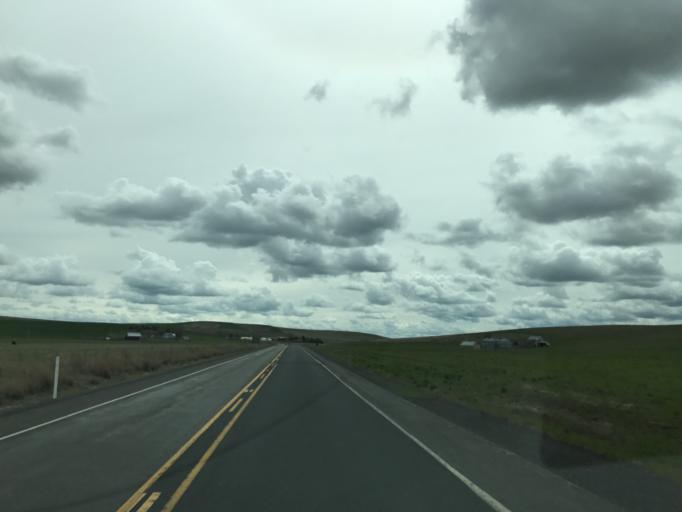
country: US
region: Washington
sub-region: Garfield County
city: Pomeroy
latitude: 46.7663
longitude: -117.7112
